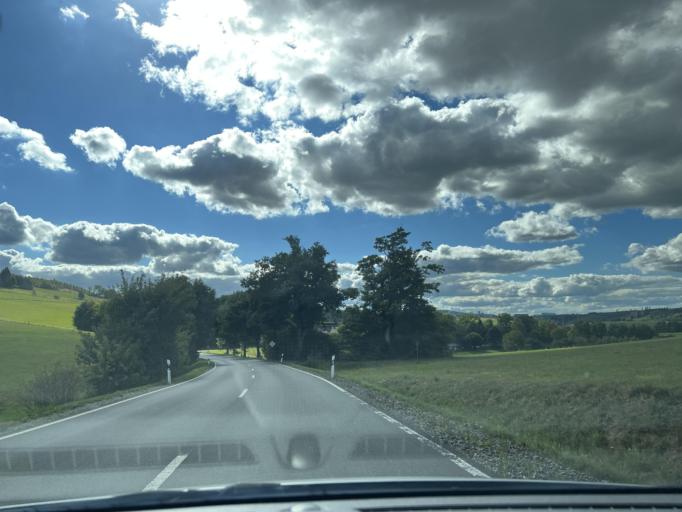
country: DE
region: North Rhine-Westphalia
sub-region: Regierungsbezirk Arnsberg
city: Bad Berleburg
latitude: 51.0076
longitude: 8.3537
